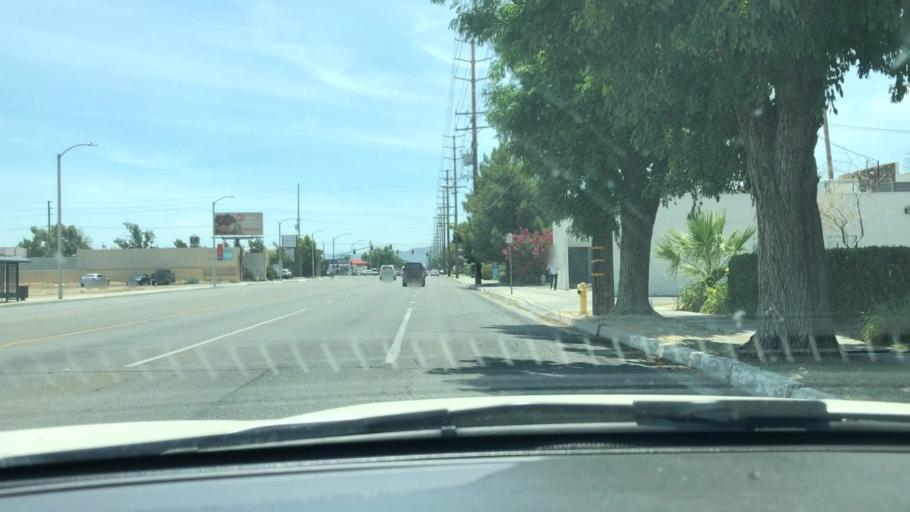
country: US
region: California
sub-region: Los Angeles County
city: Lancaster
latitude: 34.6915
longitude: -118.1482
